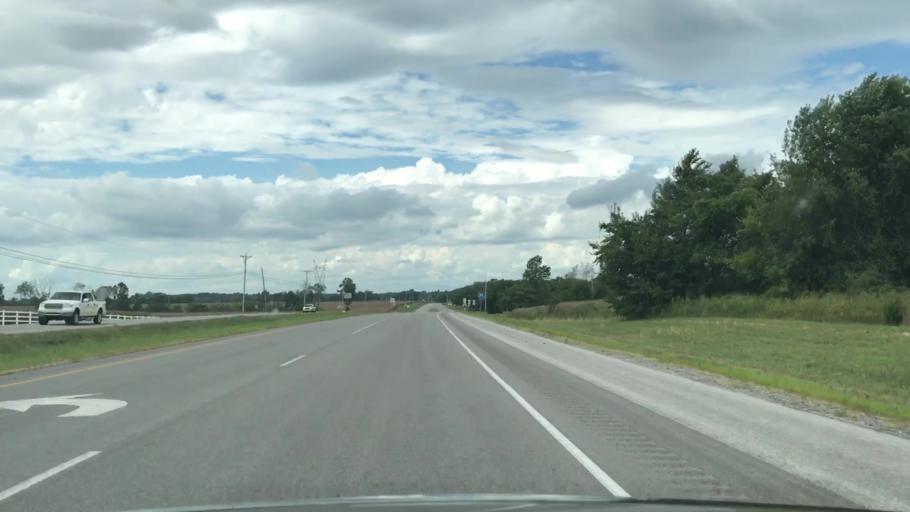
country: US
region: Kentucky
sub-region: Christian County
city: Hopkinsville
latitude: 36.8569
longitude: -87.4224
